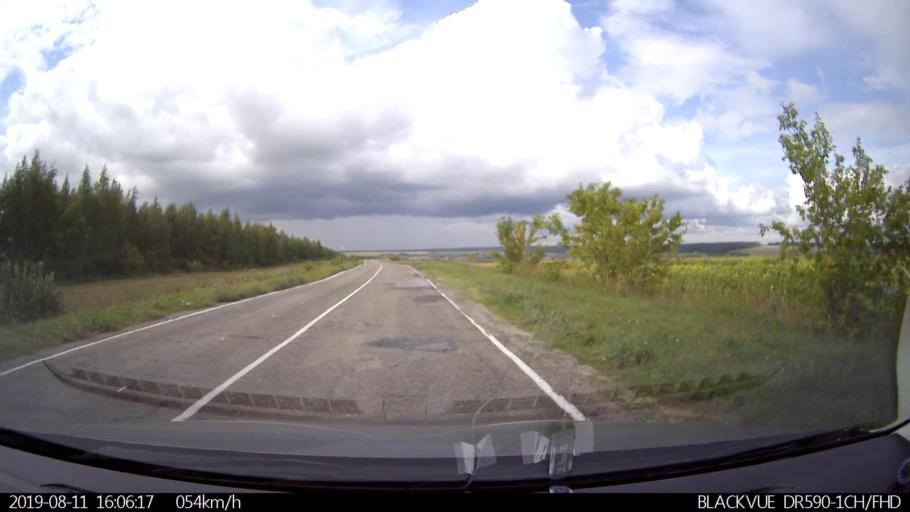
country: RU
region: Ulyanovsk
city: Ignatovka
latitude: 53.9677
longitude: 47.6490
